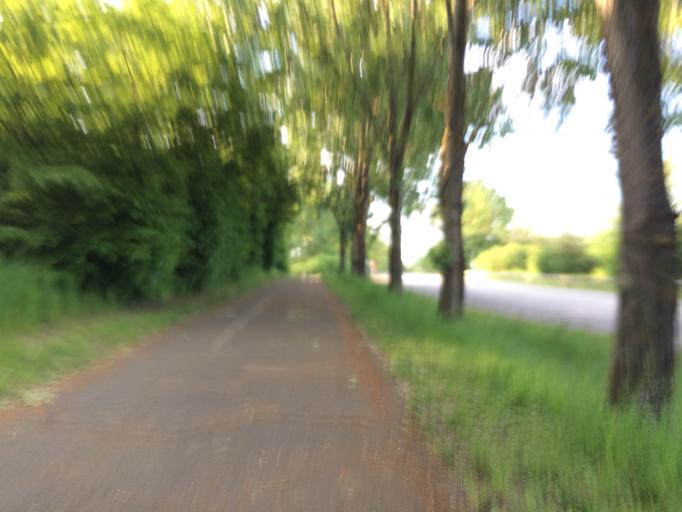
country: FR
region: Ile-de-France
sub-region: Departement de l'Essonne
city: Lisses
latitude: 48.6098
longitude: 2.4241
